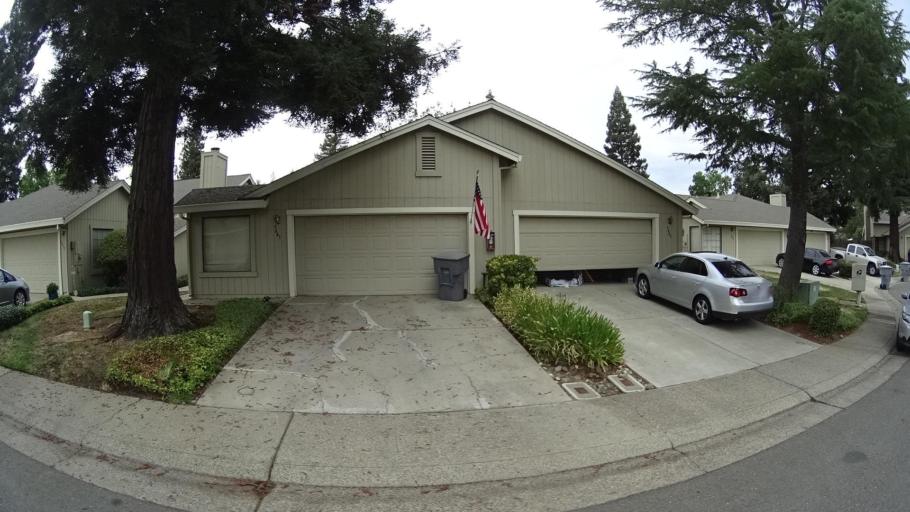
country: US
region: California
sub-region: Placer County
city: Rocklin
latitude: 38.7814
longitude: -121.2484
